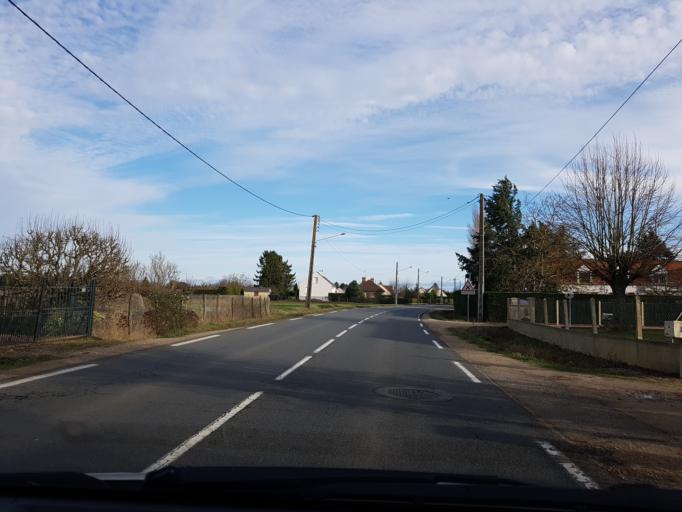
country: FR
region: Centre
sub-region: Departement du Loiret
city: Sandillon
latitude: 47.8523
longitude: 2.0101
